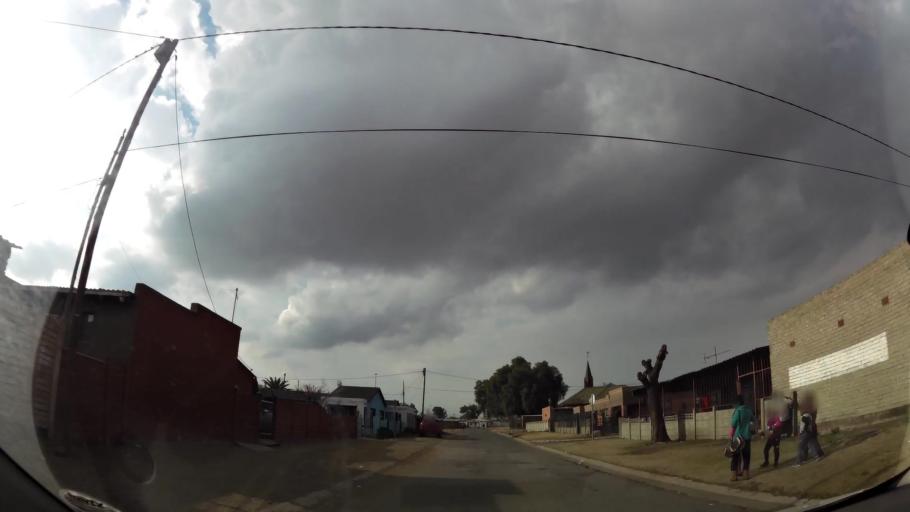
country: ZA
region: Orange Free State
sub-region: Fezile Dabi District Municipality
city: Sasolburg
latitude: -26.8392
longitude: 27.8432
